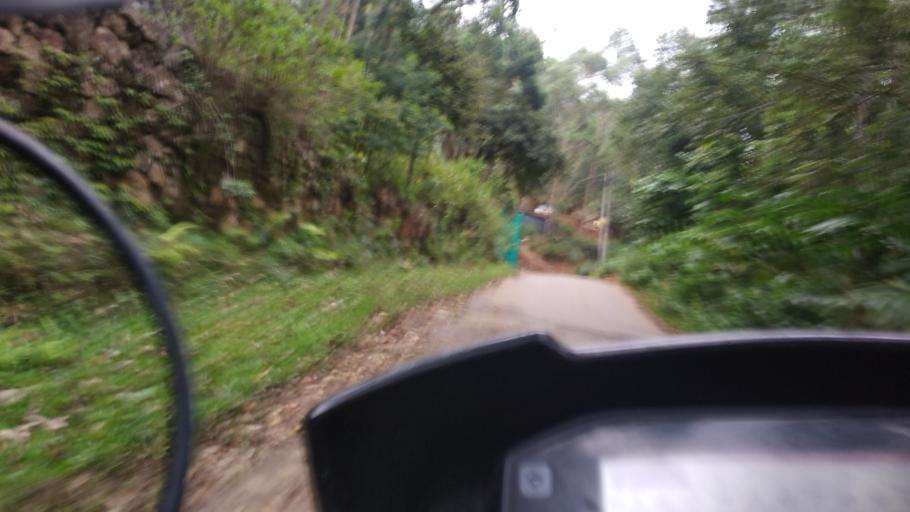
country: IN
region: Kerala
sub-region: Idukki
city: Munnar
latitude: 10.0375
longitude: 77.1724
